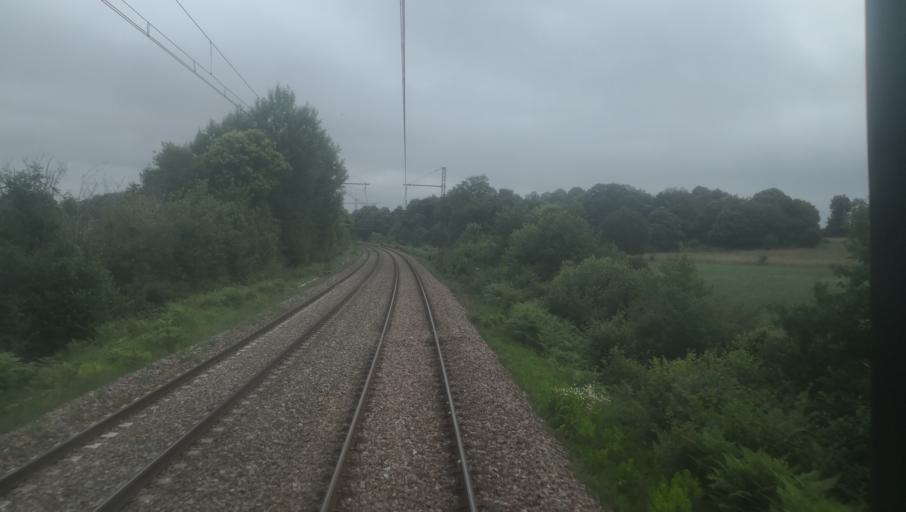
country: FR
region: Limousin
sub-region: Departement de la Creuse
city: Saint-Maurice-la-Souterraine
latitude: 46.1811
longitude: 1.4505
